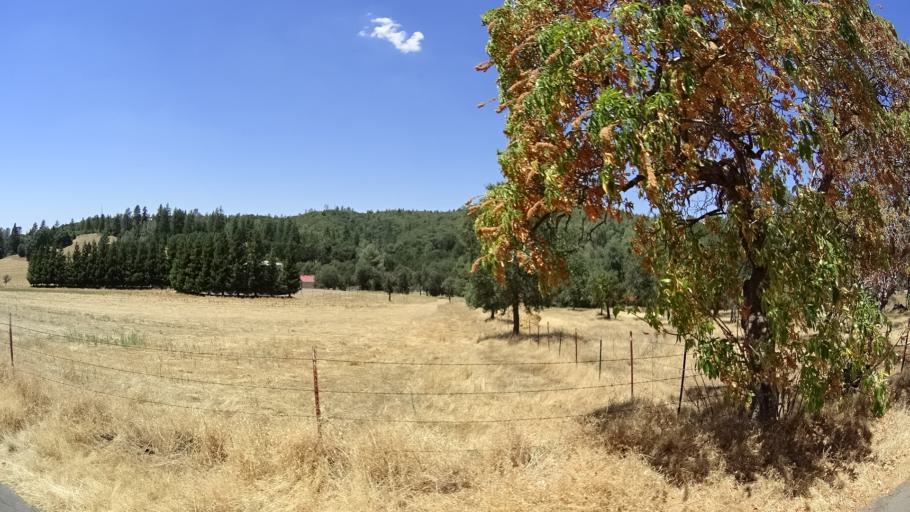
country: US
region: California
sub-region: Calaveras County
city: Murphys
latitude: 38.1148
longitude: -120.4735
